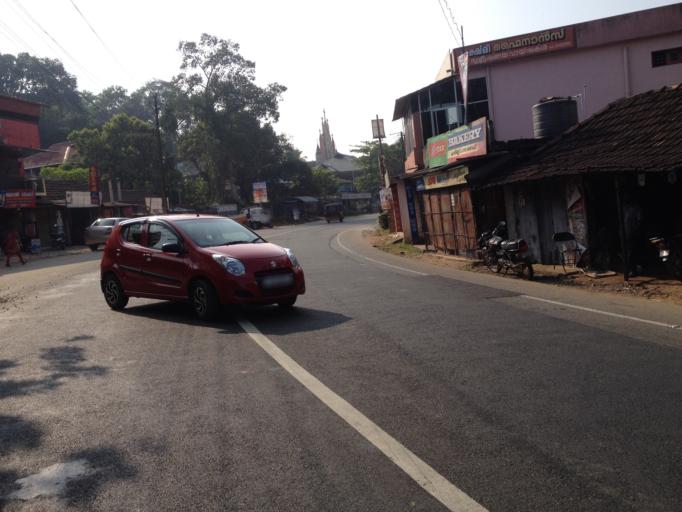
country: IN
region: Kerala
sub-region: Pattanamtitta
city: Adur
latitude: 9.1614
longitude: 76.7239
